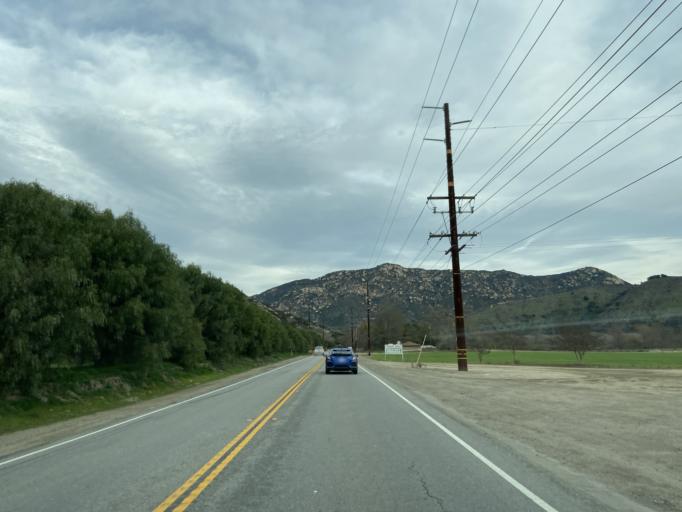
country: US
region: California
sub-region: San Diego County
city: Rainbow
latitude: 33.3437
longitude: -117.1291
